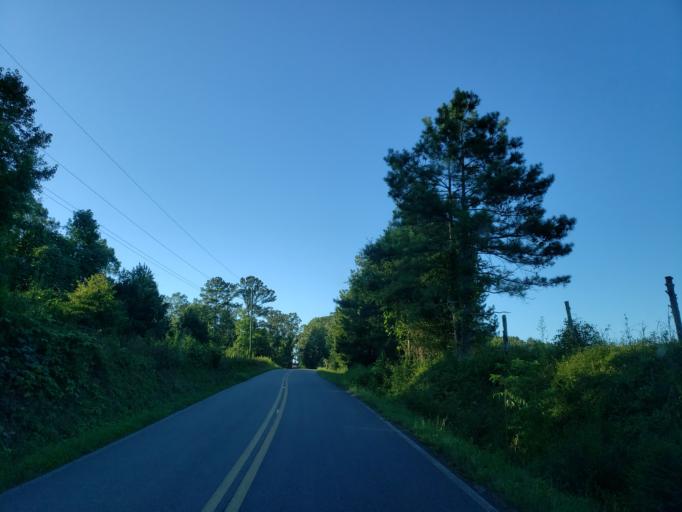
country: US
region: Georgia
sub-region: Polk County
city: Aragon
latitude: 34.0897
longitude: -85.0271
